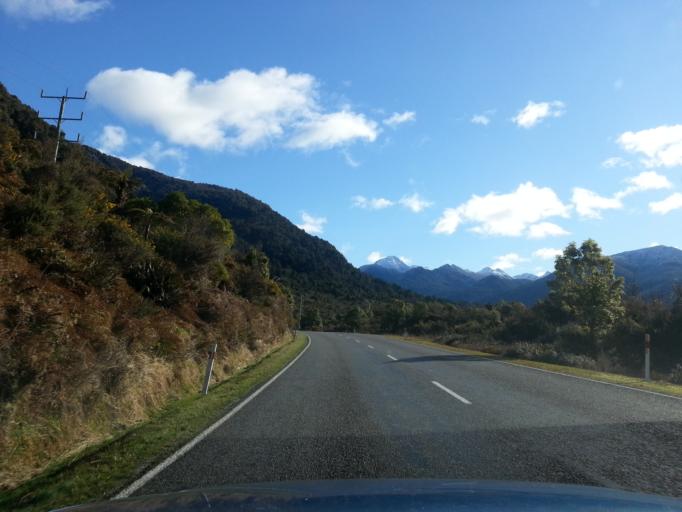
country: NZ
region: West Coast
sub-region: Grey District
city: Greymouth
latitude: -42.7418
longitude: 171.4692
